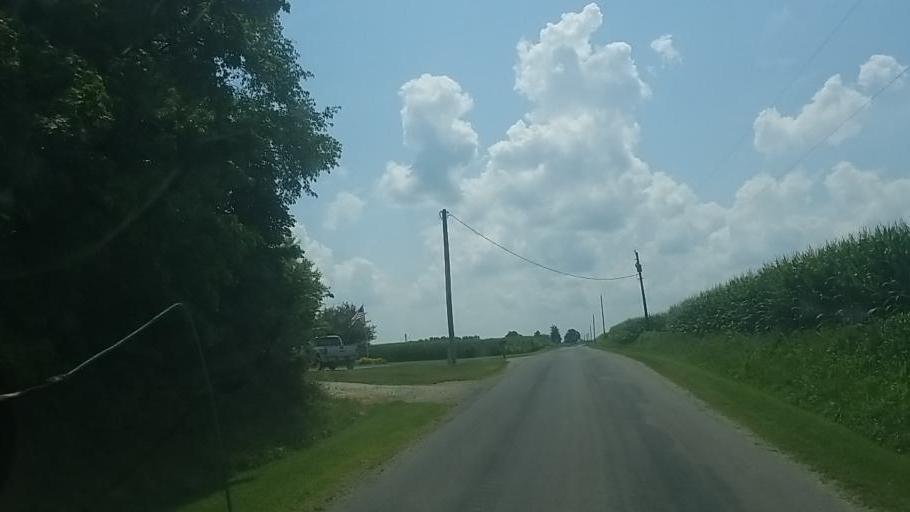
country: US
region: Ohio
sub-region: Marion County
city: Marion
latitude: 40.7241
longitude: -83.1499
